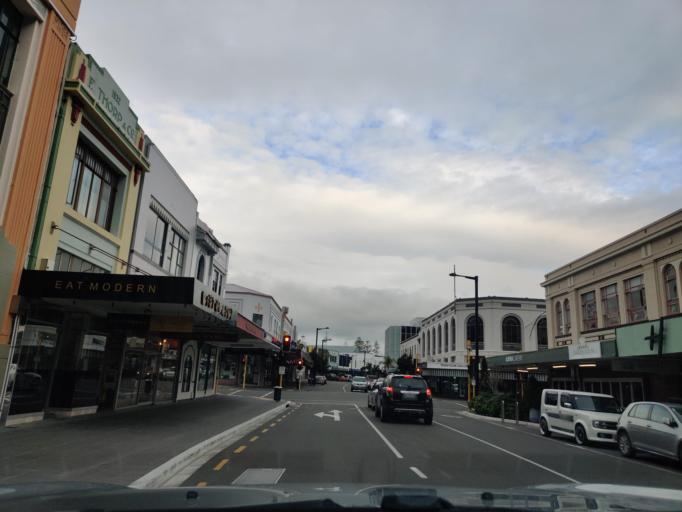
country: NZ
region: Hawke's Bay
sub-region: Napier City
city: Napier
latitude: -39.4891
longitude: 176.9179
